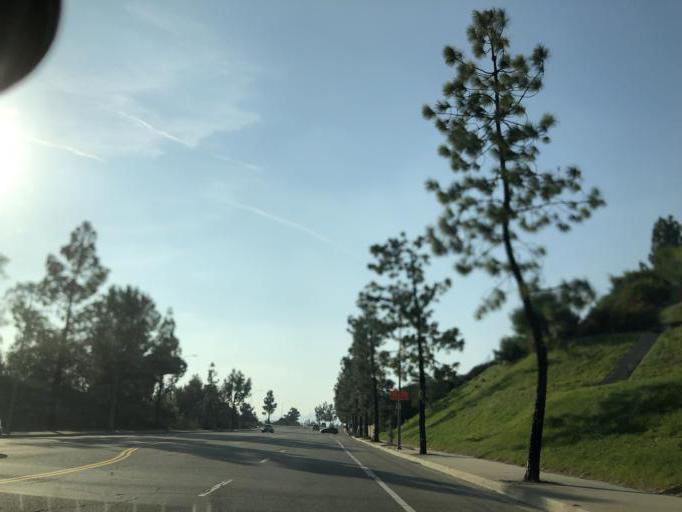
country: US
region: California
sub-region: Los Angeles County
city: Northridge
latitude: 34.2756
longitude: -118.5390
